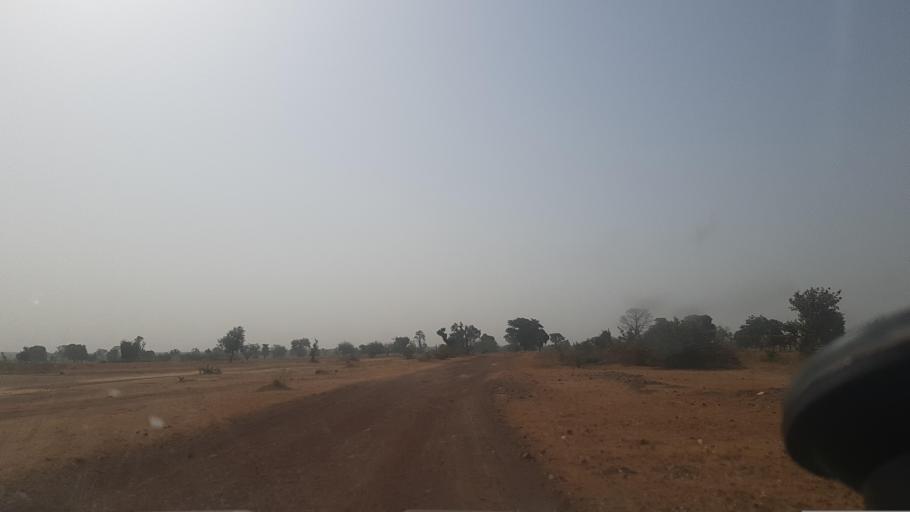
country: ML
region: Segou
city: Baroueli
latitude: 13.1527
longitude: -6.5164
